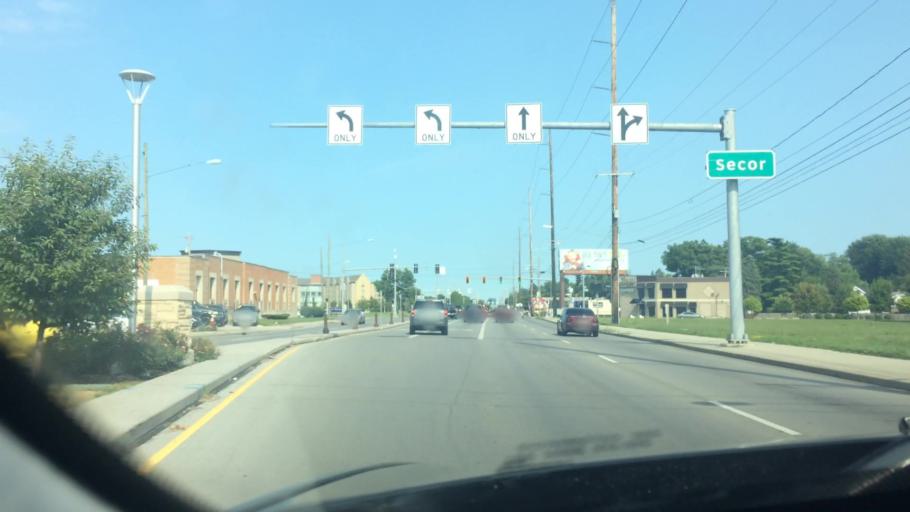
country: US
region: Ohio
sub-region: Lucas County
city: Ottawa Hills
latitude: 41.6528
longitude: -83.6236
